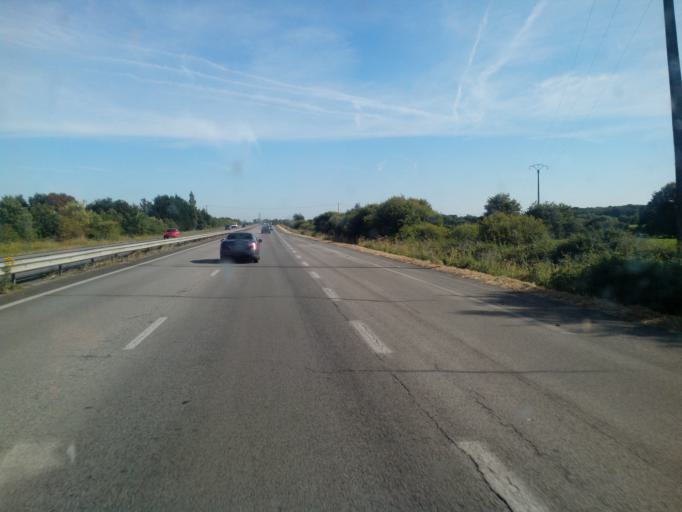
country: FR
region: Pays de la Loire
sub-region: Departement de la Loire-Atlantique
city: Heric
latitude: 47.4433
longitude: -1.6408
